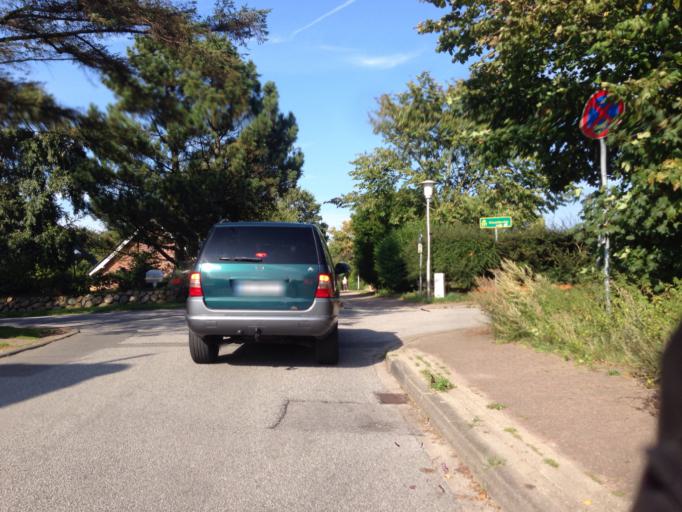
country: DE
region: Schleswig-Holstein
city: Westerland
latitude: 54.9076
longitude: 8.3189
